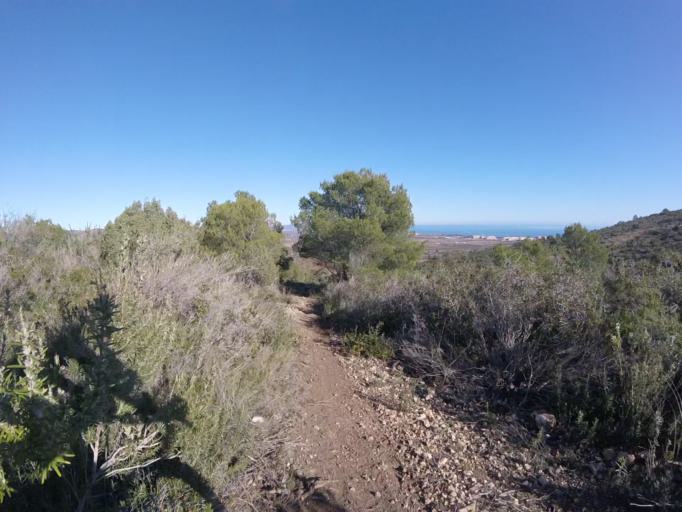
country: ES
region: Valencia
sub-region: Provincia de Castello
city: Orpesa/Oropesa del Mar
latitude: 40.1126
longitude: 0.1168
